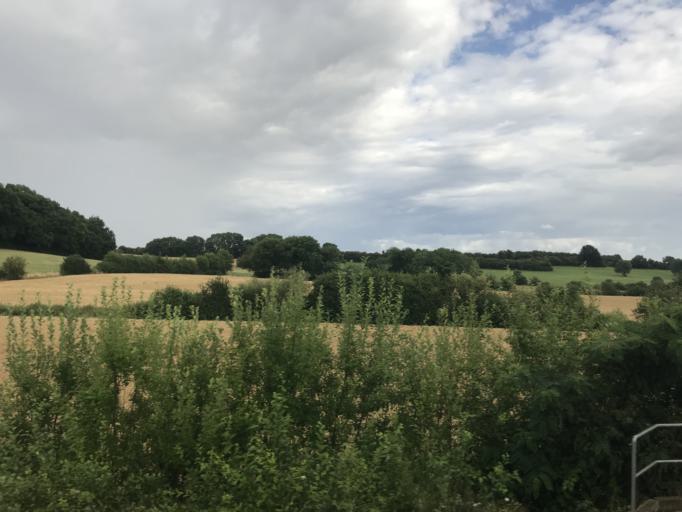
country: LU
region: Luxembourg
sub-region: Canton d'Esch-sur-Alzette
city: Reckange-sur-Mess
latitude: 49.5745
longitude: 6.0019
